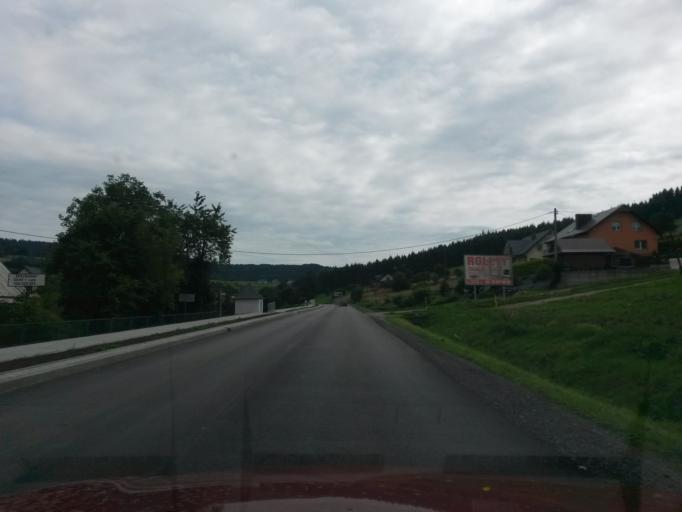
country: PL
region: Lesser Poland Voivodeship
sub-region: Powiat nowosadecki
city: Labowa
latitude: 49.4992
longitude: 20.9006
